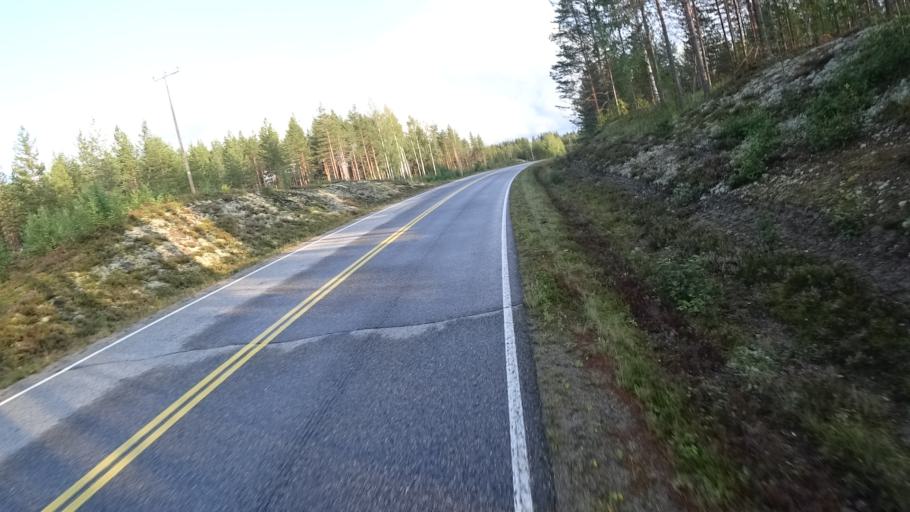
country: FI
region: North Karelia
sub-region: Joensuu
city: Ilomantsi
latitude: 62.6337
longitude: 31.0928
